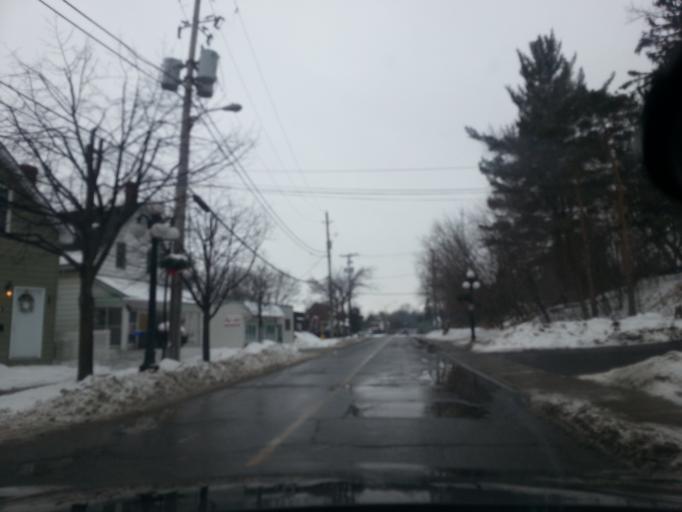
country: CA
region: Ontario
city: Bells Corners
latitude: 45.3445
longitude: -76.0358
